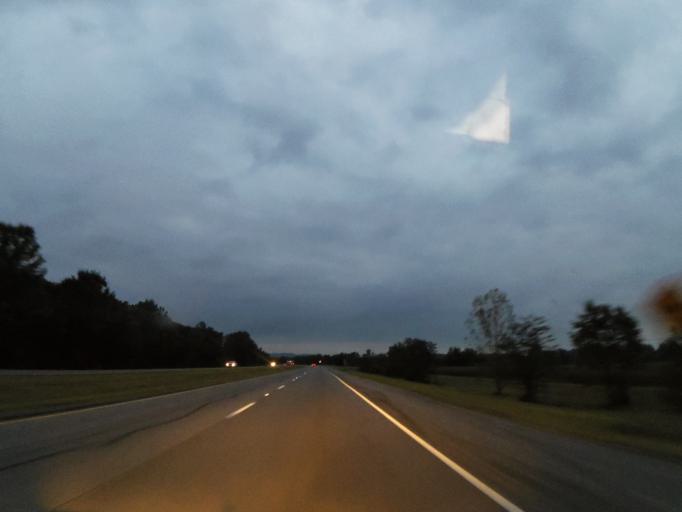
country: US
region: Alabama
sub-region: Madison County
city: New Hope
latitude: 34.6314
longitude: -86.3145
